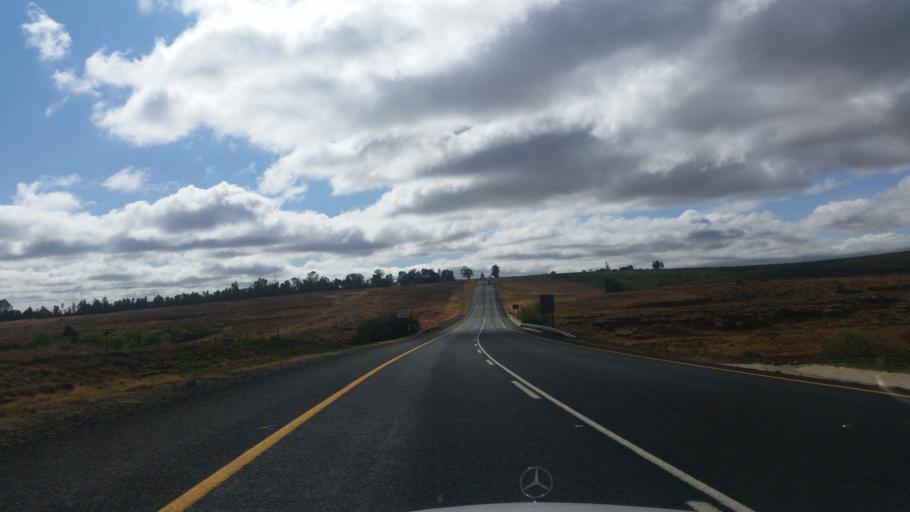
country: ZA
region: Orange Free State
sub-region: Thabo Mofutsanyana District Municipality
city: Phuthaditjhaba
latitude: -28.2957
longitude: 28.8034
